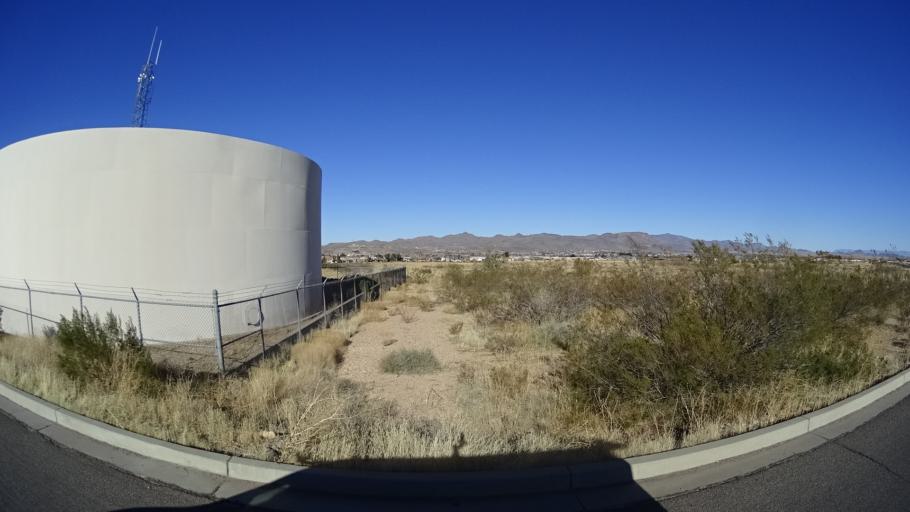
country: US
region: Arizona
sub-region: Mohave County
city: Kingman
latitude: 35.1850
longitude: -114.0029
